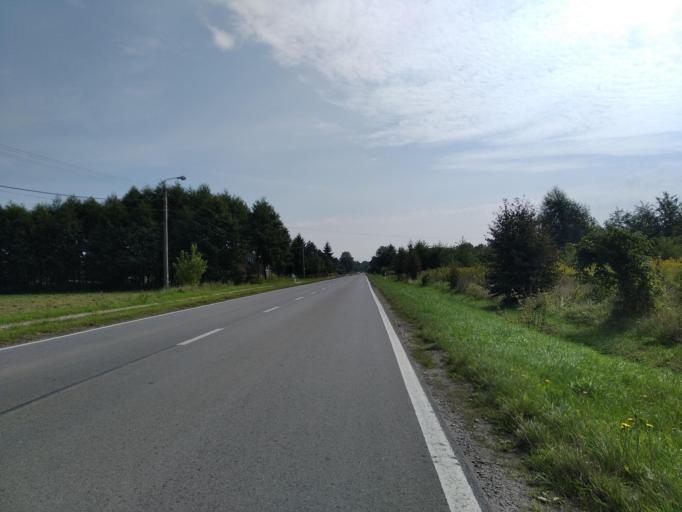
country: PL
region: Subcarpathian Voivodeship
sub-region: Powiat mielecki
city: Przeclaw
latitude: 50.1627
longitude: 21.5223
